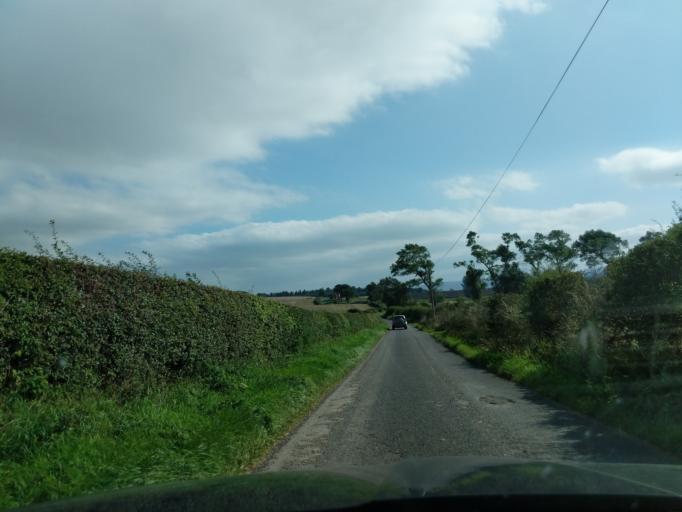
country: GB
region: England
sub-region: Northumberland
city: Ford
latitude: 55.6528
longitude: -2.1457
